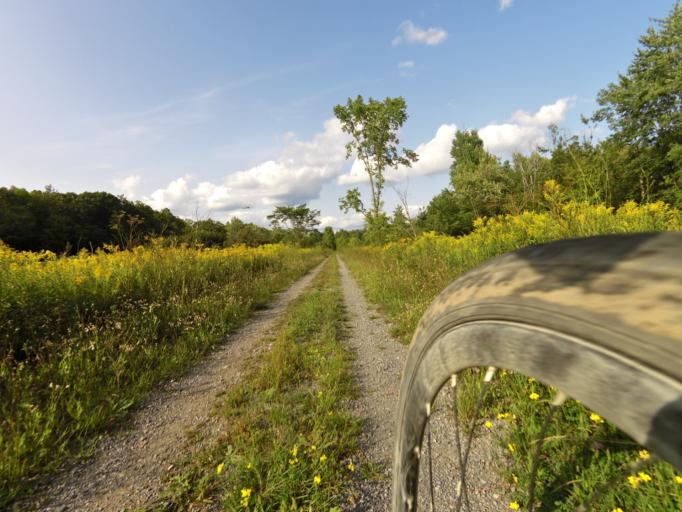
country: CA
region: Ontario
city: Kingston
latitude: 44.4450
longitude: -76.5279
